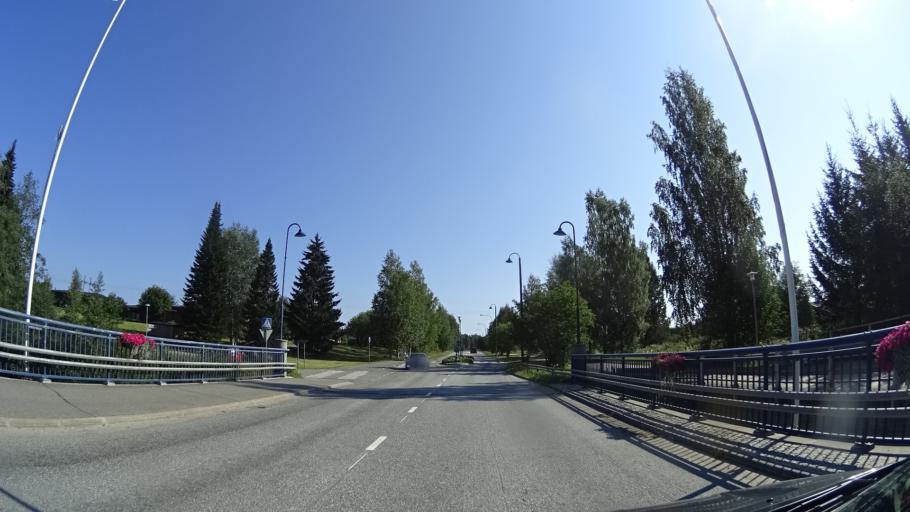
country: FI
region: North Karelia
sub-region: Joensuu
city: Juuka
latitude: 63.2451
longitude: 29.2603
